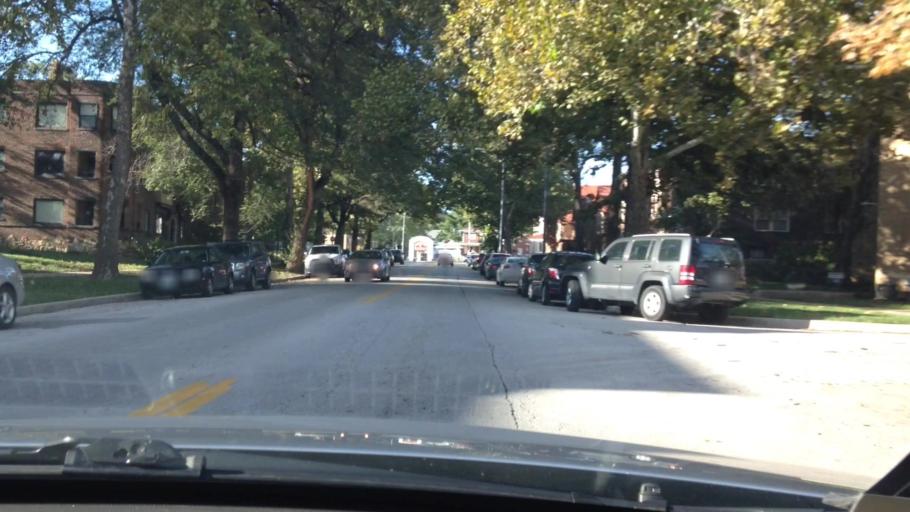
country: US
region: Kansas
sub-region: Johnson County
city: Westwood
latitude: 39.0484
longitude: -94.6018
